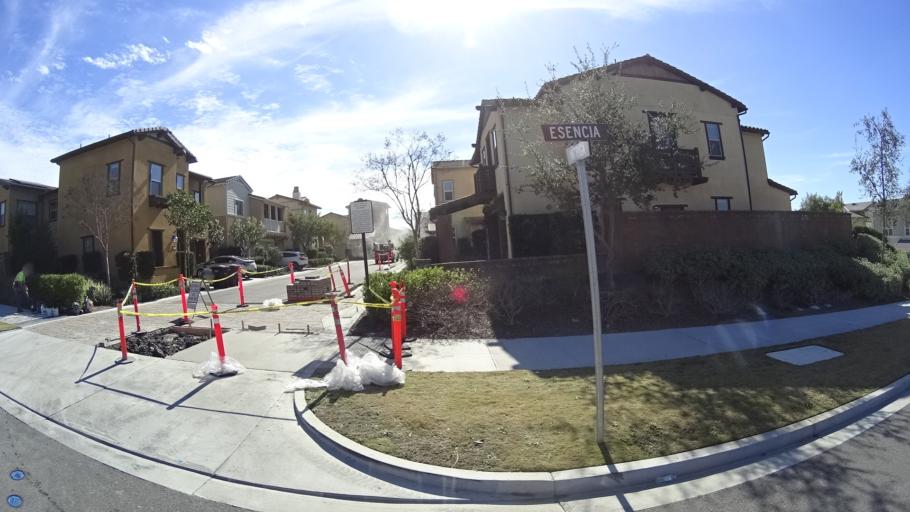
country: US
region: California
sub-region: Orange County
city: Ladera Ranch
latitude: 33.5378
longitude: -117.6010
